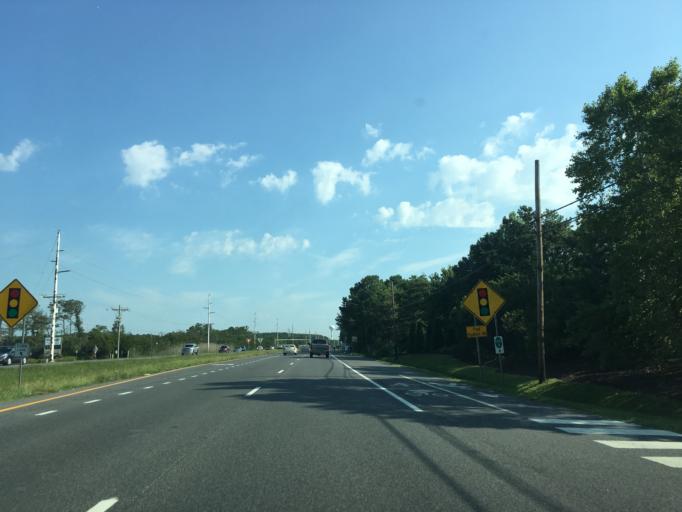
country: US
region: Delaware
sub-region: Sussex County
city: Bethany Beach
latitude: 38.5517
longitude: -75.0593
